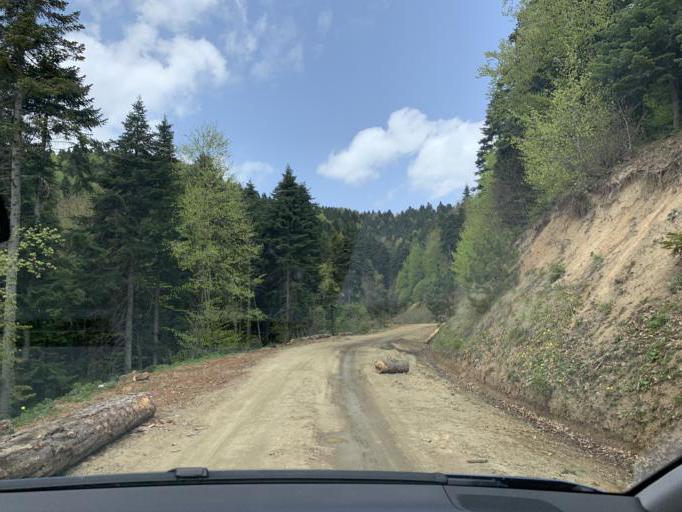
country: TR
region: Bolu
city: Bolu
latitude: 40.8382
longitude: 31.6686
